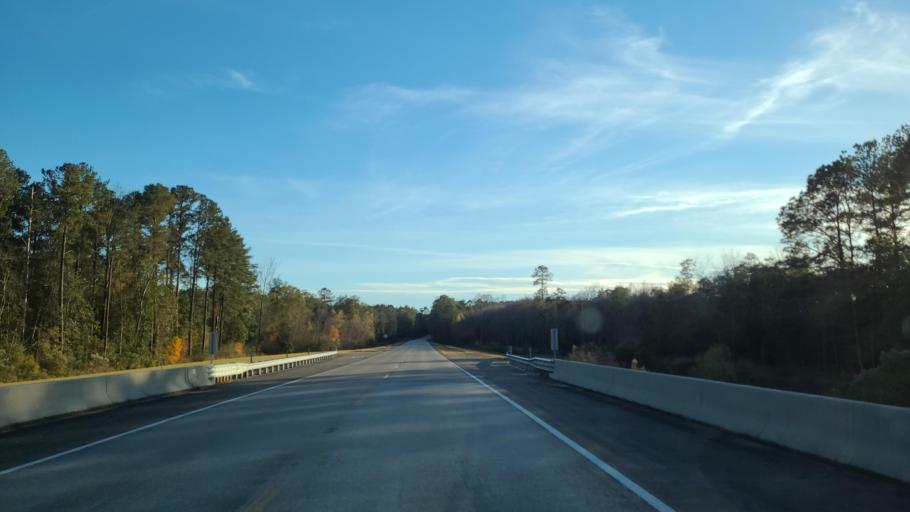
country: US
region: Mississippi
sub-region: Lamar County
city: Purvis
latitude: 31.0849
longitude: -89.4168
